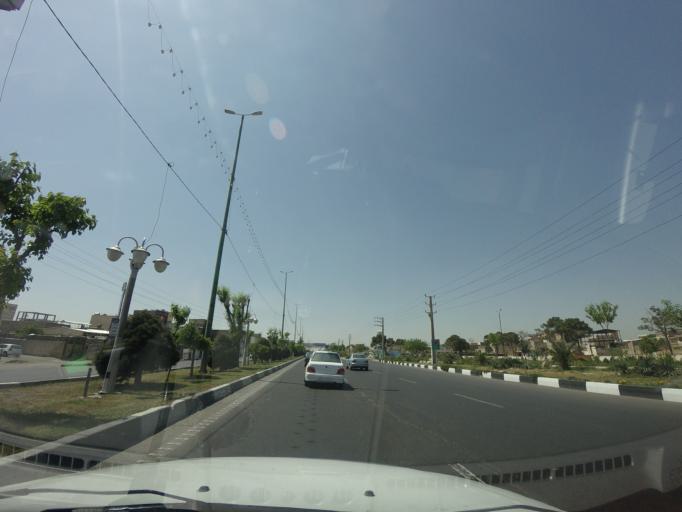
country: IR
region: Tehran
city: Eslamshahr
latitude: 35.5896
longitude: 51.2885
